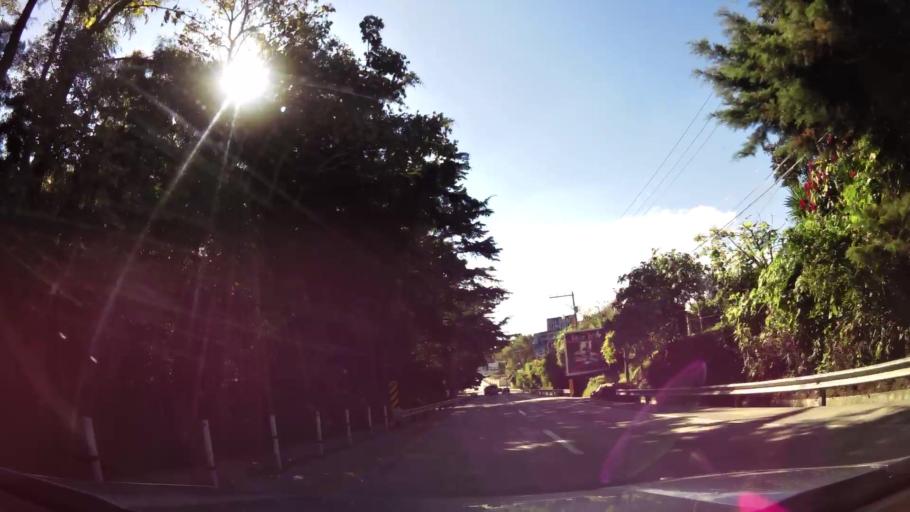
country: GT
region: Sacatepequez
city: Santa Lucia Milpas Altas
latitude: 14.5783
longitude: -90.6702
